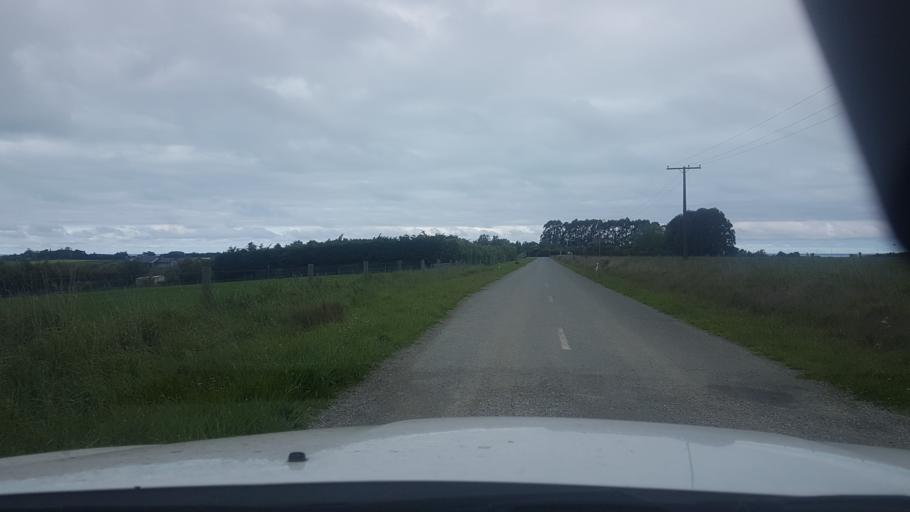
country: NZ
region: Canterbury
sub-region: Timaru District
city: Timaru
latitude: -44.4462
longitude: 171.2081
